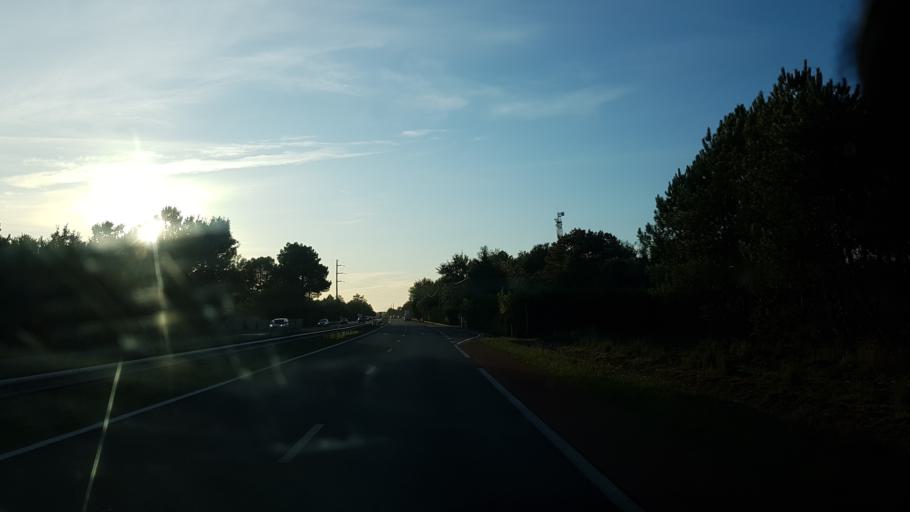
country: FR
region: Aquitaine
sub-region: Departement de la Gironde
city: Andernos-les-Bains
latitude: 44.7777
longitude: -1.0417
